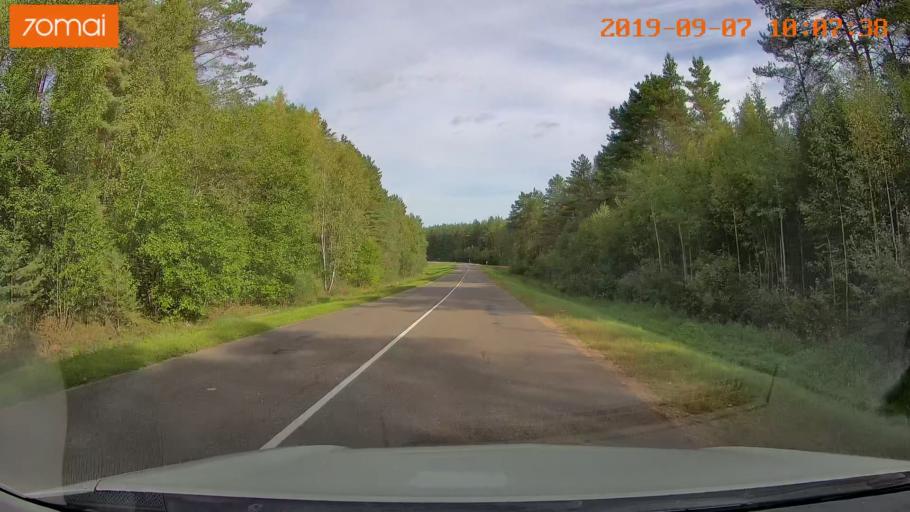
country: BY
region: Grodnenskaya
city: Voranava
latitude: 54.0782
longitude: 25.3959
